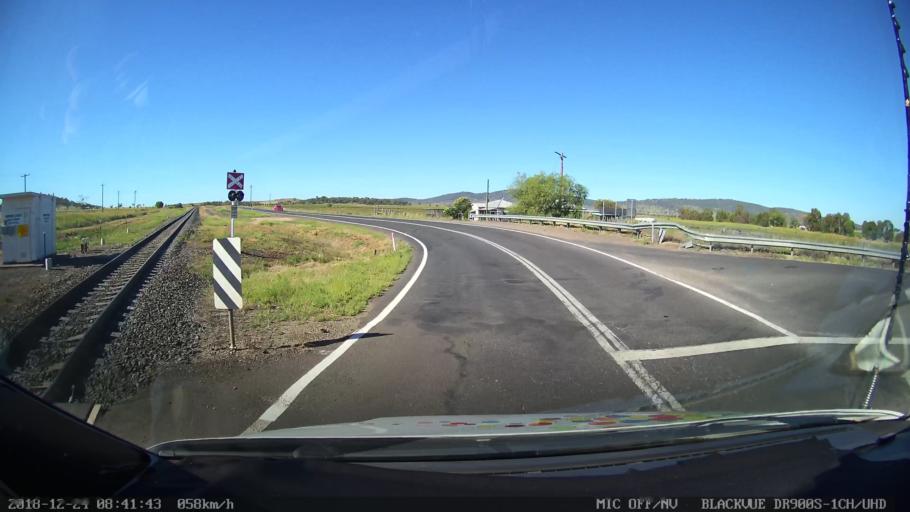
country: AU
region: New South Wales
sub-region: Liverpool Plains
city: Quirindi
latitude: -31.3660
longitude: 150.6444
